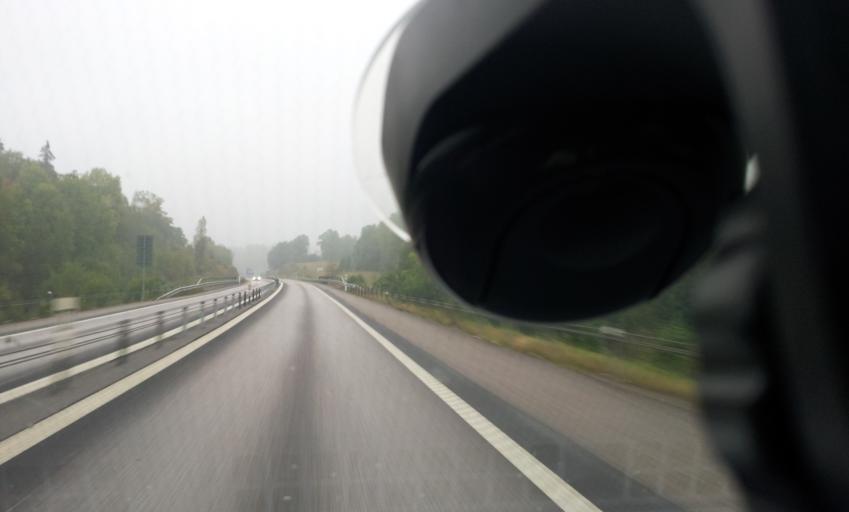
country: SE
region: OEstergoetland
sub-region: Valdemarsviks Kommun
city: Gusum
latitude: 58.2725
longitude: 16.5171
